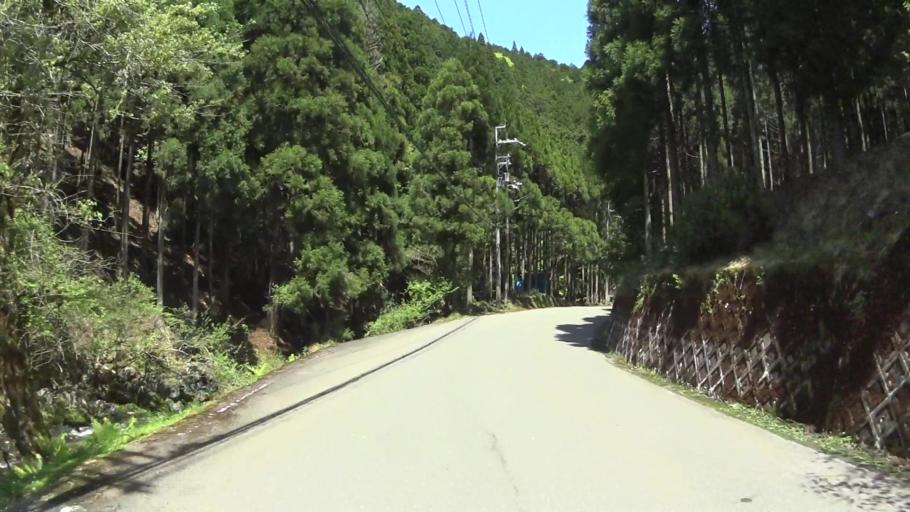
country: JP
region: Shiga Prefecture
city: Kitahama
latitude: 35.1891
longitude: 135.7847
